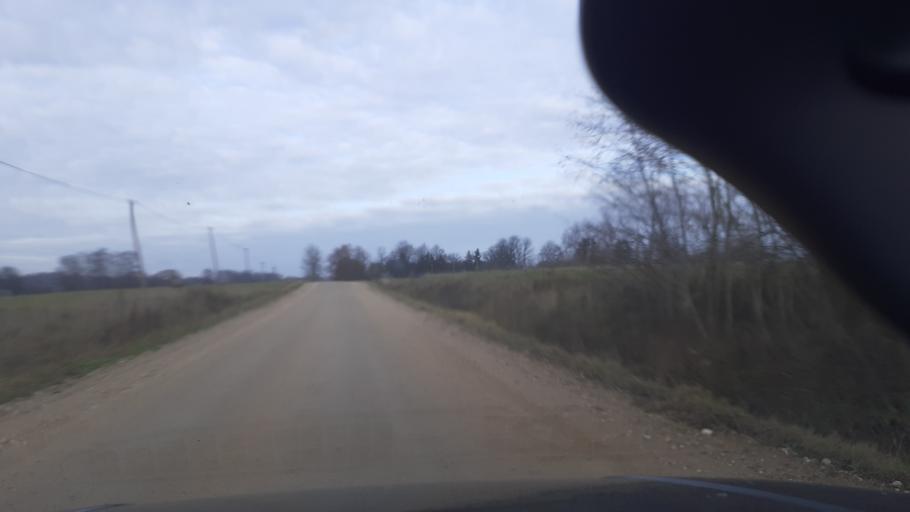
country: LV
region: Alsunga
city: Alsunga
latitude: 56.9062
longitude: 21.6552
